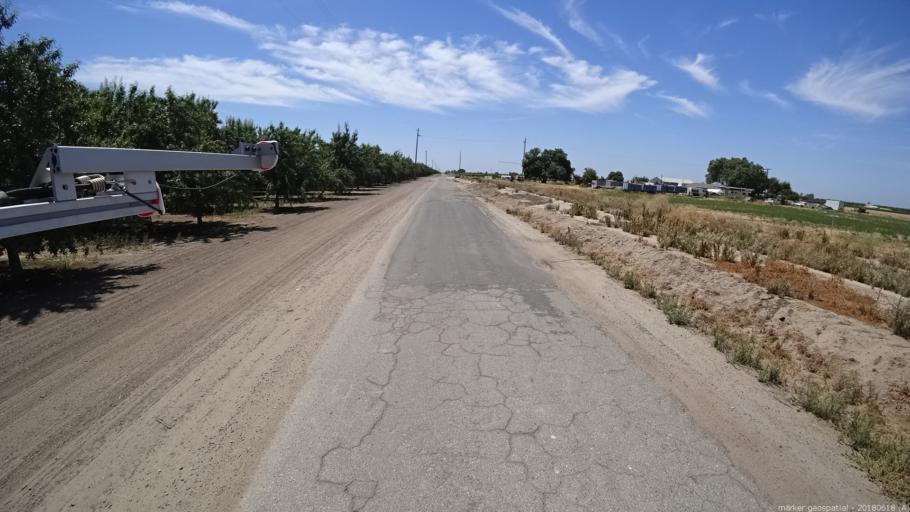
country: US
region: California
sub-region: Madera County
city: Parkwood
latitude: 36.8910
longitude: -120.1014
